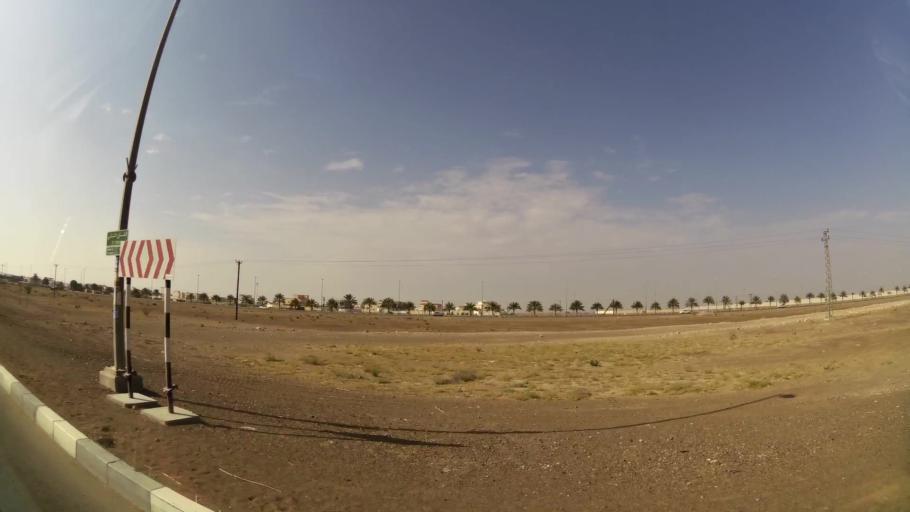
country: AE
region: Abu Dhabi
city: Al Ain
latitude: 24.0905
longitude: 55.8629
